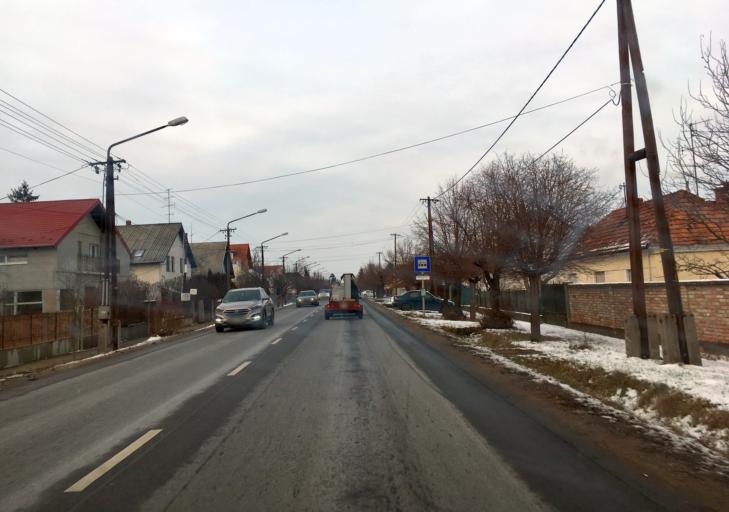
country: HU
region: Gyor-Moson-Sopron
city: Mosonmagyarovar
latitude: 47.8619
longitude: 17.2670
